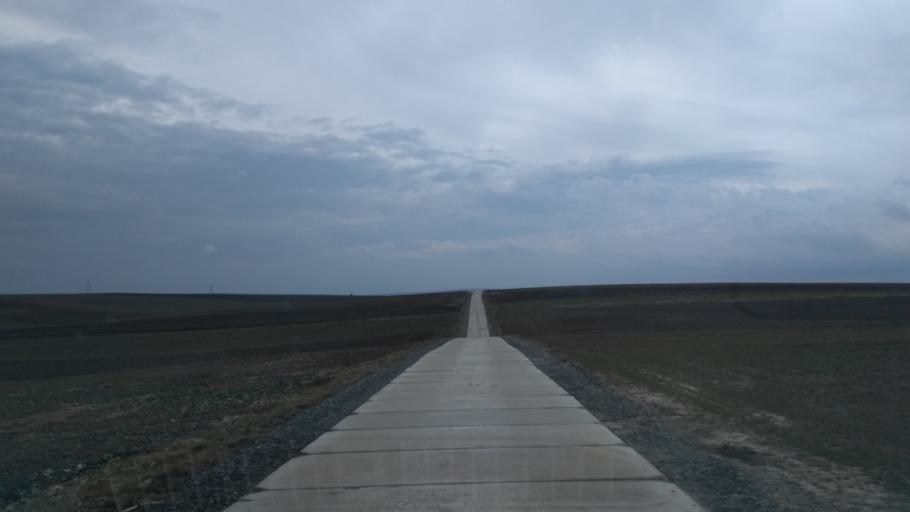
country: PL
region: Subcarpathian Voivodeship
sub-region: Powiat jaroslawski
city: Rokietnica
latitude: 49.9350
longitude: 22.5910
